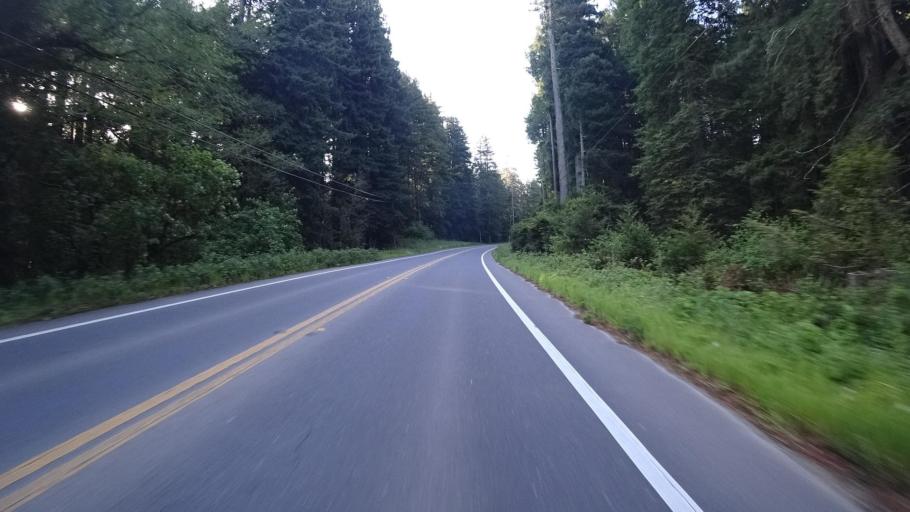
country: US
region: California
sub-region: Humboldt County
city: Myrtletown
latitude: 40.7783
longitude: -124.0746
